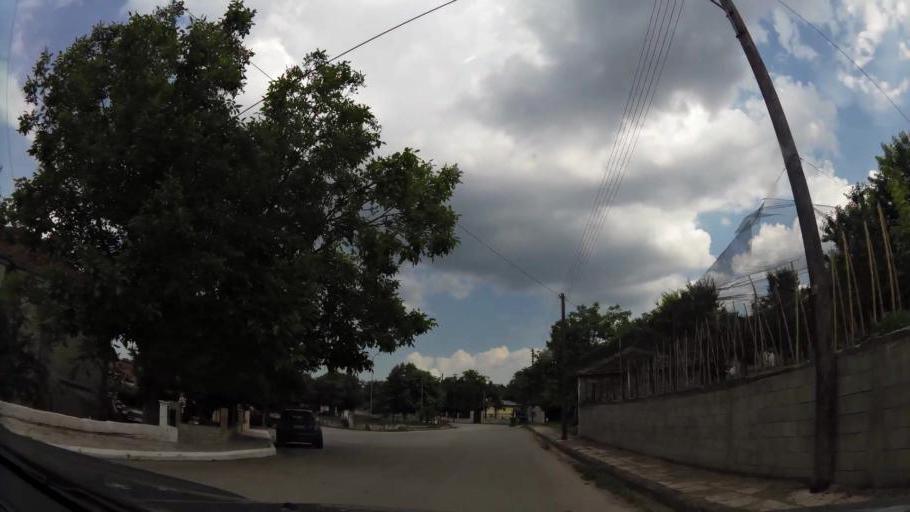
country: GR
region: West Macedonia
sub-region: Nomos Kozanis
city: Koila
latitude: 40.3479
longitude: 21.8388
